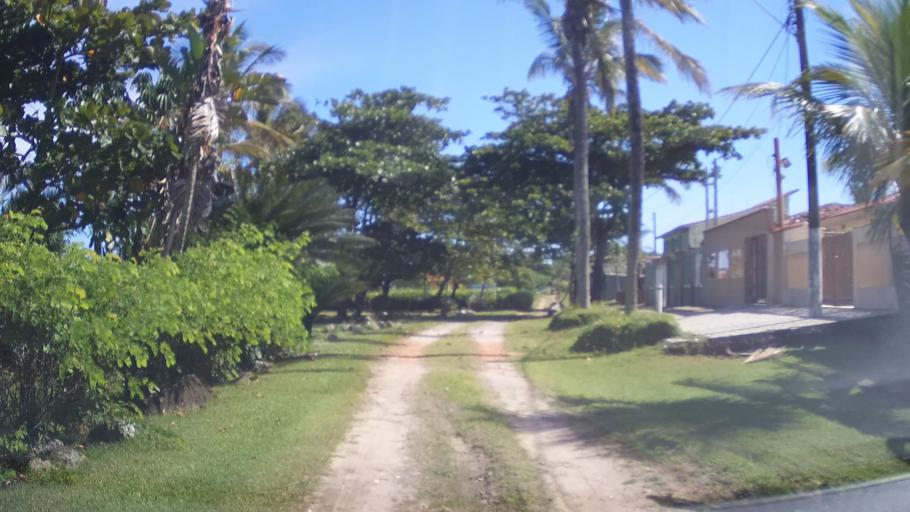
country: BR
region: Sao Paulo
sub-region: Itanhaem
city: Itanhaem
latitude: -24.1608
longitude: -46.7413
